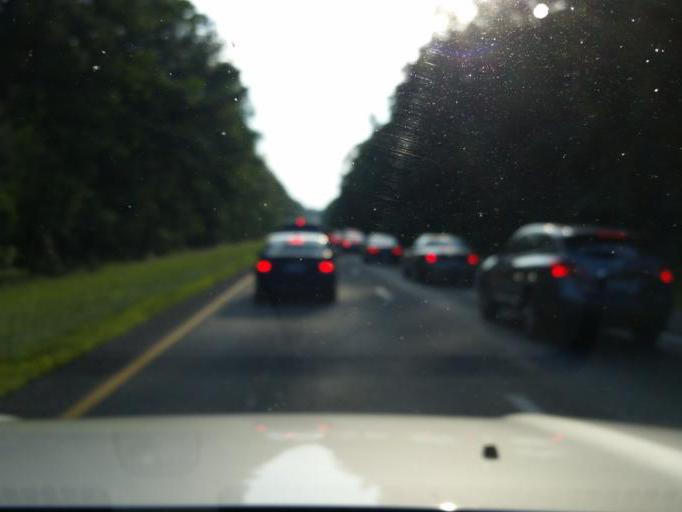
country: US
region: Virginia
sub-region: New Kent County
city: New Kent
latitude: 37.5093
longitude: -77.1267
